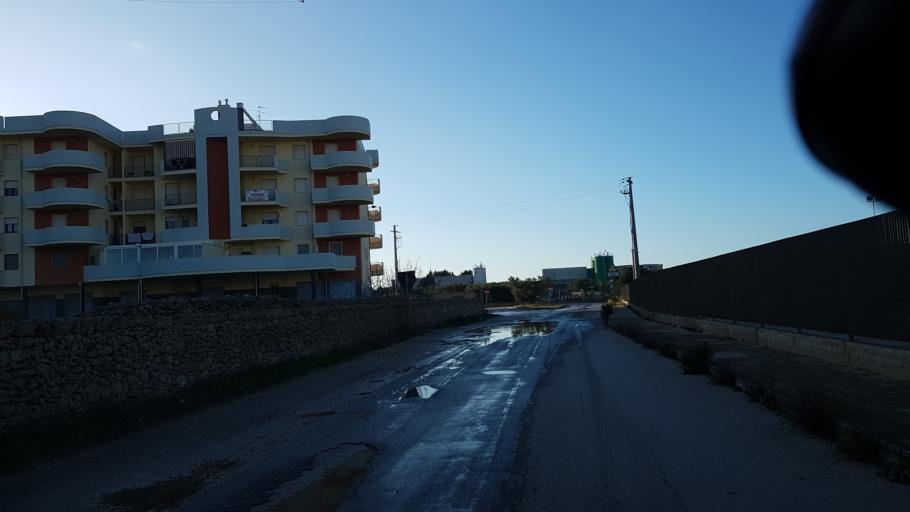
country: IT
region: Apulia
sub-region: Provincia di Bari
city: Gioia del Colle
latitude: 40.8018
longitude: 16.9056
